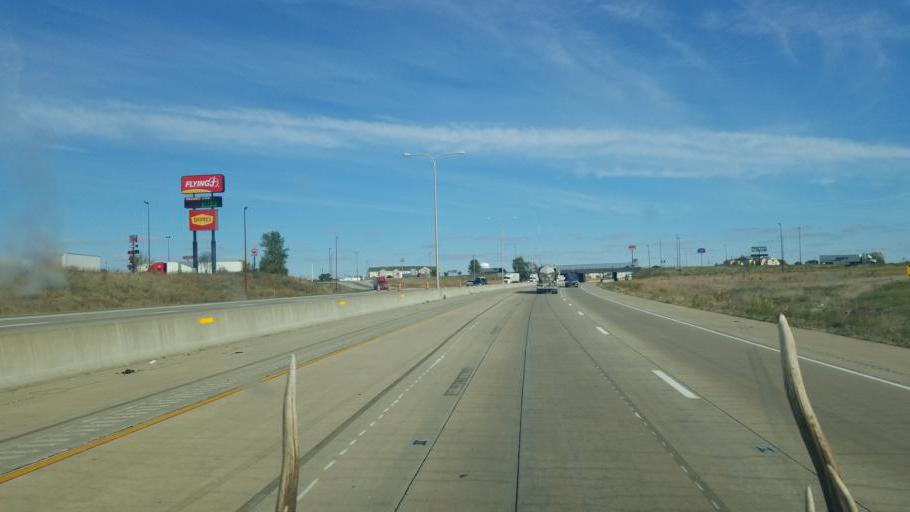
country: US
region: Illinois
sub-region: Effingham County
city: Effingham
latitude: 39.1312
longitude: -88.5649
